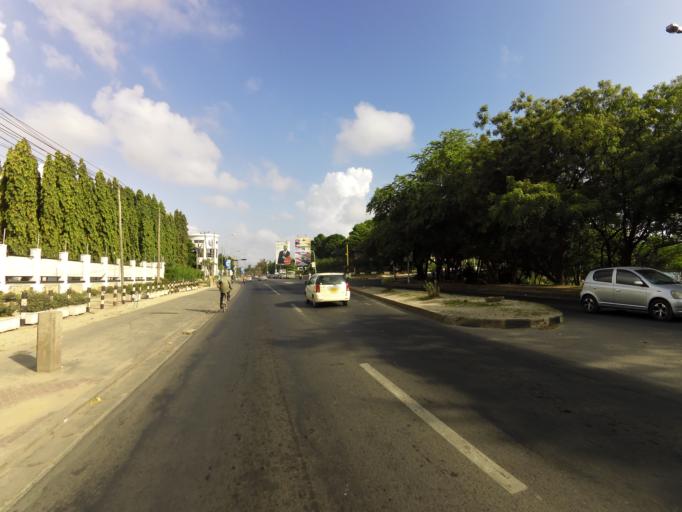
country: TZ
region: Dar es Salaam
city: Magomeni
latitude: -6.7918
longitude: 39.2799
